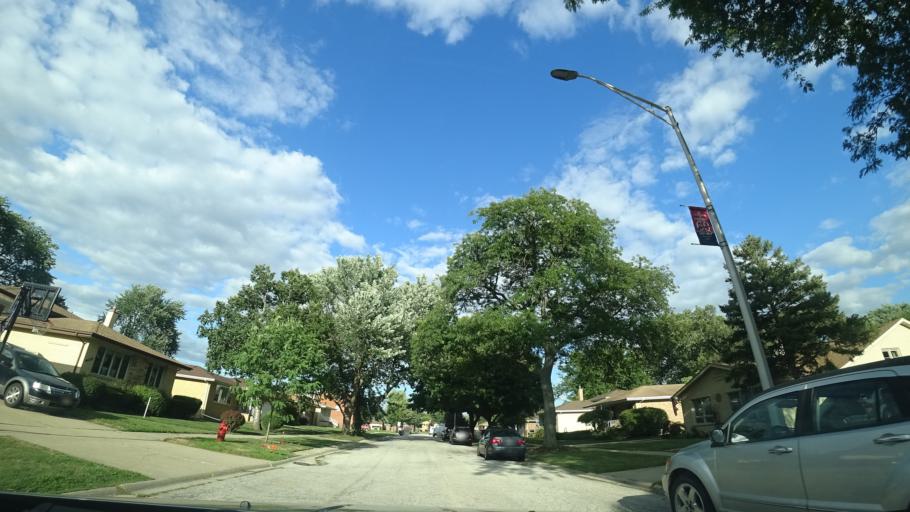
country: US
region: Illinois
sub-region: Cook County
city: Merrionette Park
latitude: 41.7013
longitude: -87.7225
